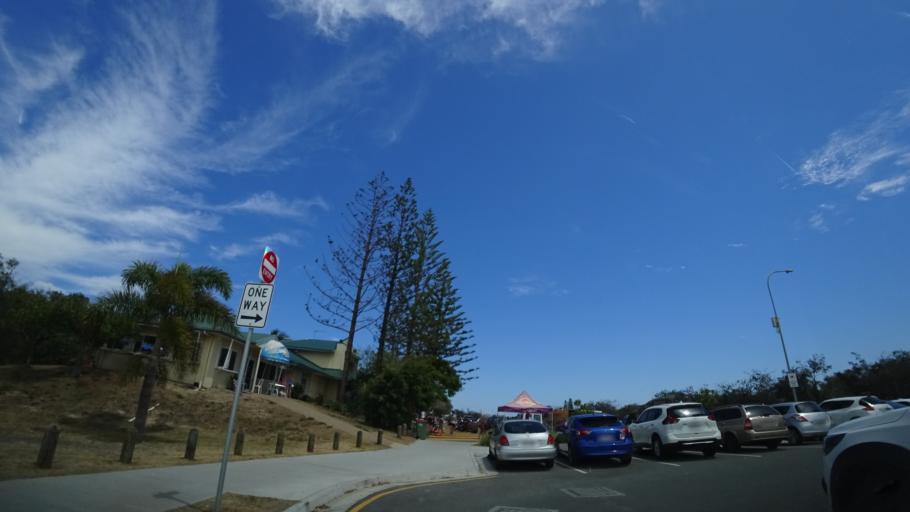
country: AU
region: Queensland
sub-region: Gold Coast
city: Southport
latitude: -27.9376
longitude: 153.4264
